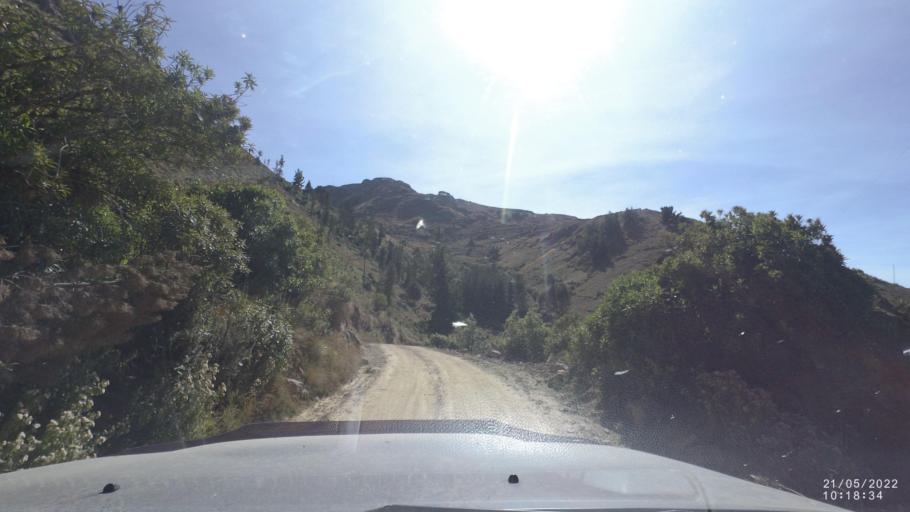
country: BO
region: Cochabamba
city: Colomi
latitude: -17.3272
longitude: -65.9608
